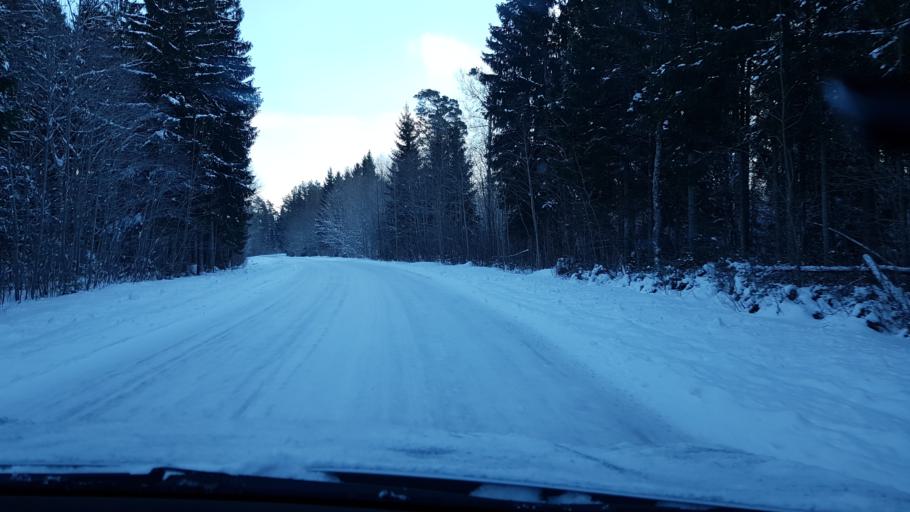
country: EE
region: Harju
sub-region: Nissi vald
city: Turba
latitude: 59.1456
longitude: 24.1534
